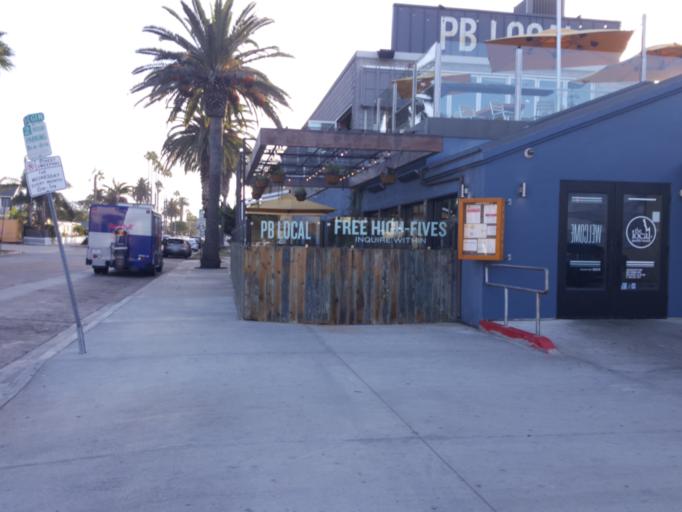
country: US
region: California
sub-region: San Diego County
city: La Jolla
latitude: 32.7937
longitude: -117.2544
